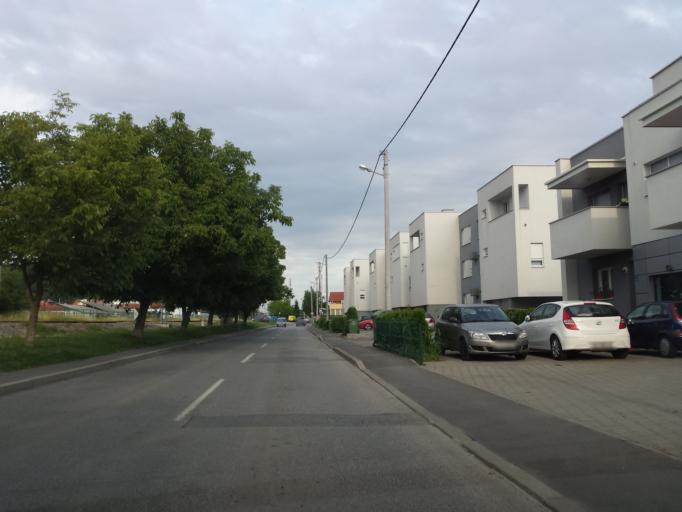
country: HR
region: Grad Zagreb
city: Jankomir
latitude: 45.8118
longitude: 15.9028
